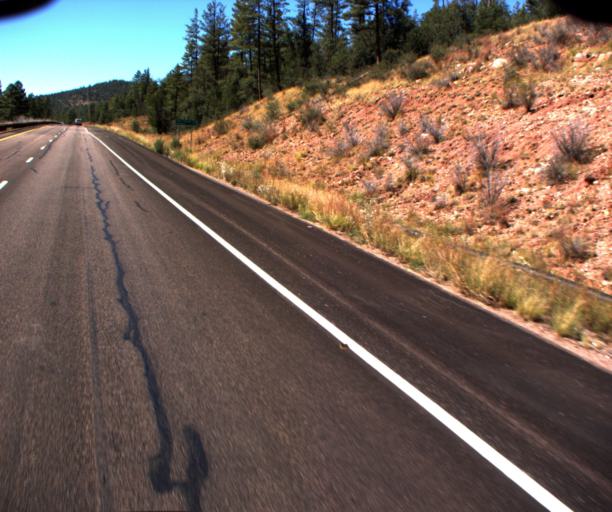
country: US
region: Arizona
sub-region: Gila County
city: Star Valley
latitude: 34.3288
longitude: -111.0962
